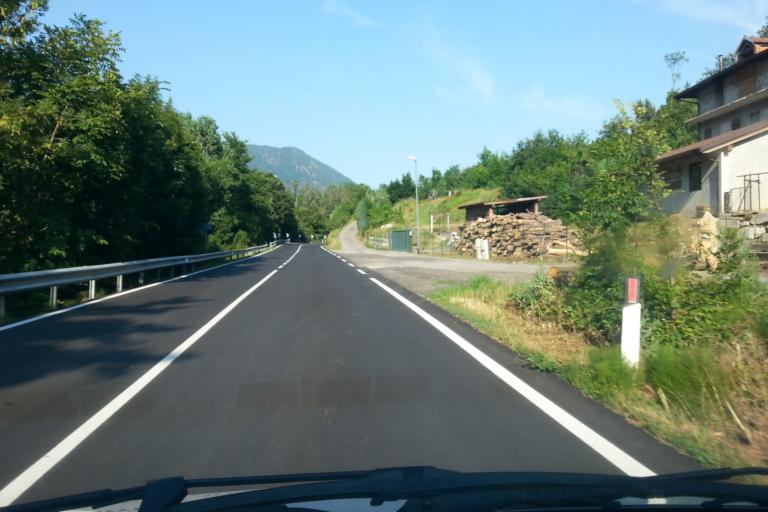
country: IT
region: Piedmont
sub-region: Provincia di Torino
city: Bruzolo
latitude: 45.1214
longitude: 7.1980
